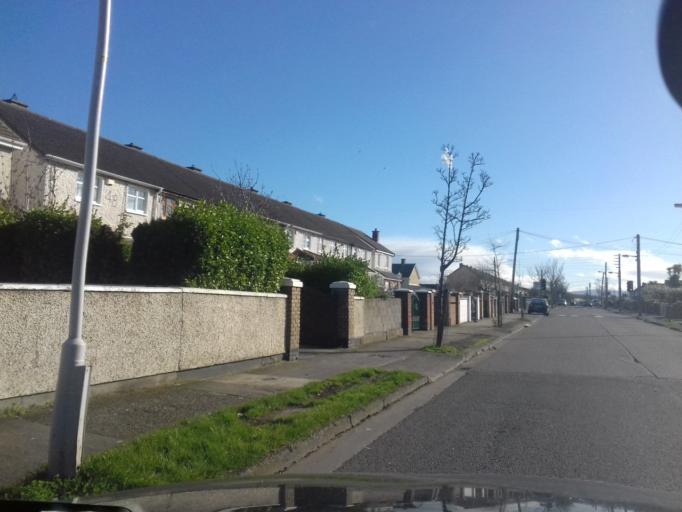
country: IE
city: Bonnybrook
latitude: 53.4000
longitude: -6.2054
